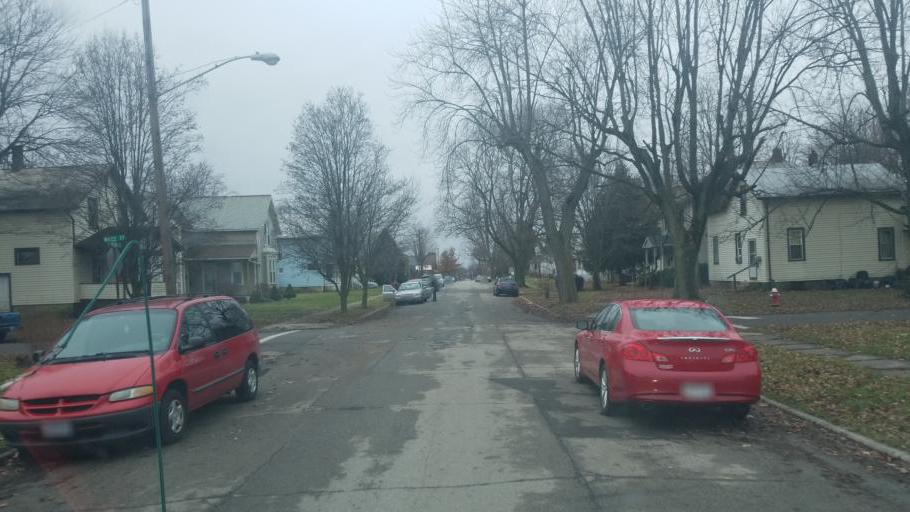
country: US
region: Ohio
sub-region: Crawford County
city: Bucyrus
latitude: 40.8065
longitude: -82.9681
